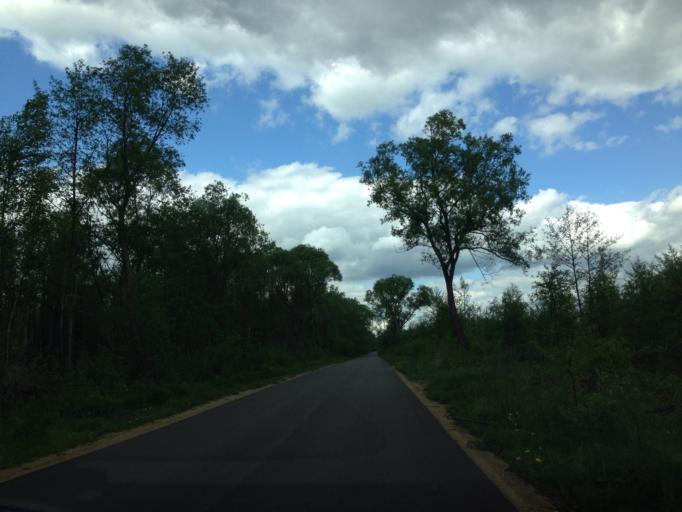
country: PL
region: Podlasie
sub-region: Powiat bialostocki
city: Tykocin
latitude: 53.3124
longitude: 22.6028
